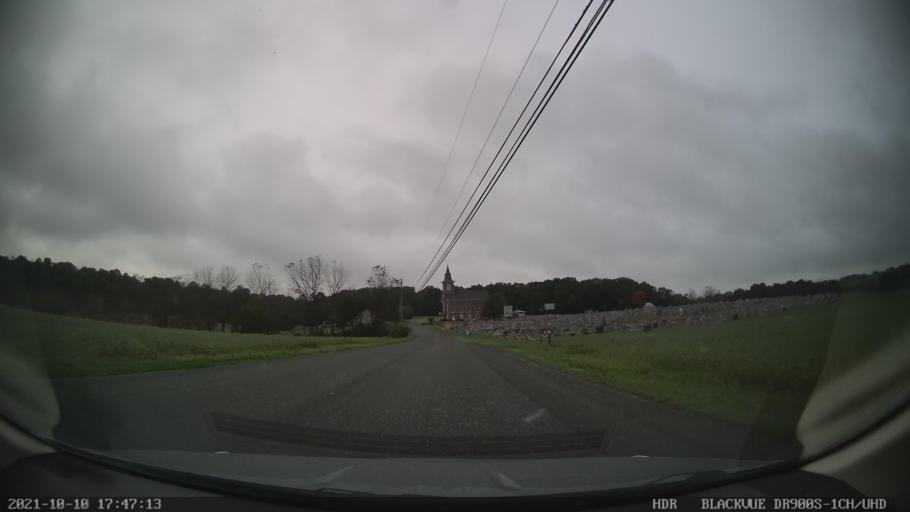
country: US
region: Pennsylvania
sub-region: Lehigh County
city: Breinigsville
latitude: 40.5720
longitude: -75.6797
